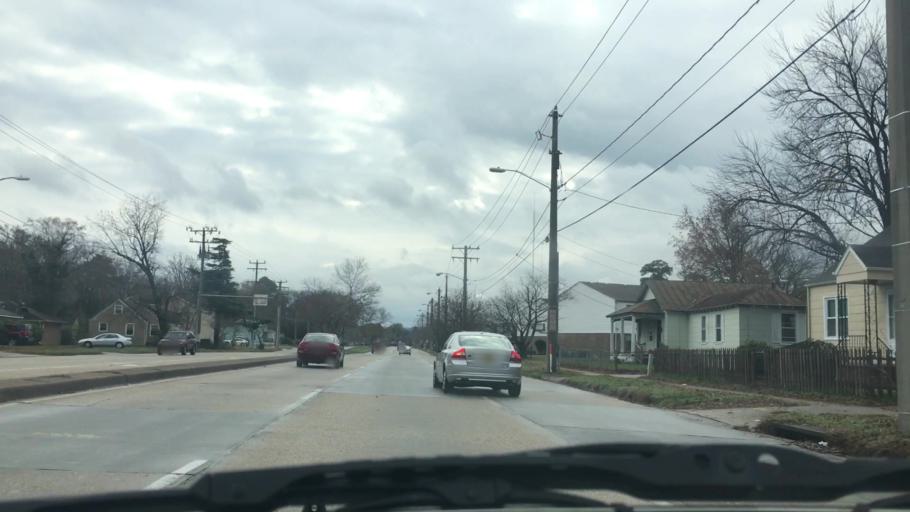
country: US
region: Virginia
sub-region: City of Norfolk
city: Norfolk
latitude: 36.8966
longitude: -76.2387
